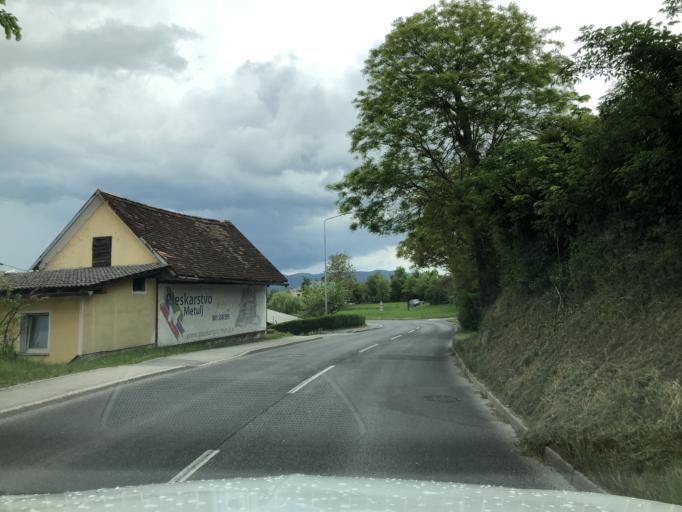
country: SI
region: Cerknica
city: Rakek
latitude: 45.8101
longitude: 14.3261
